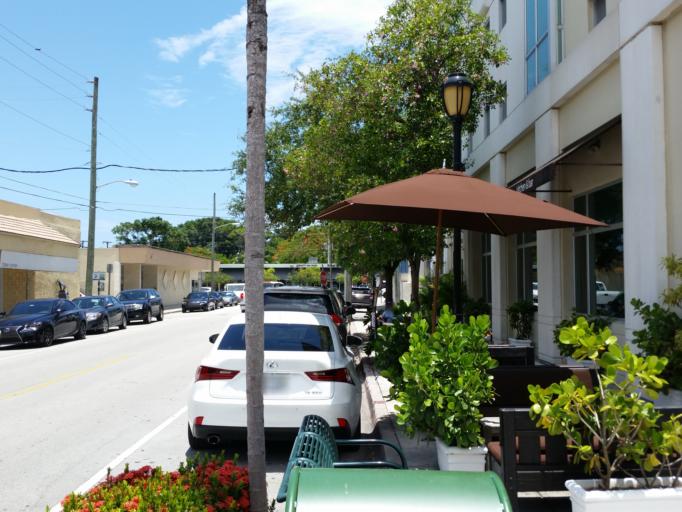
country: US
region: Florida
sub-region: Miami-Dade County
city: South Miami
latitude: 25.7035
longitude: -80.2863
